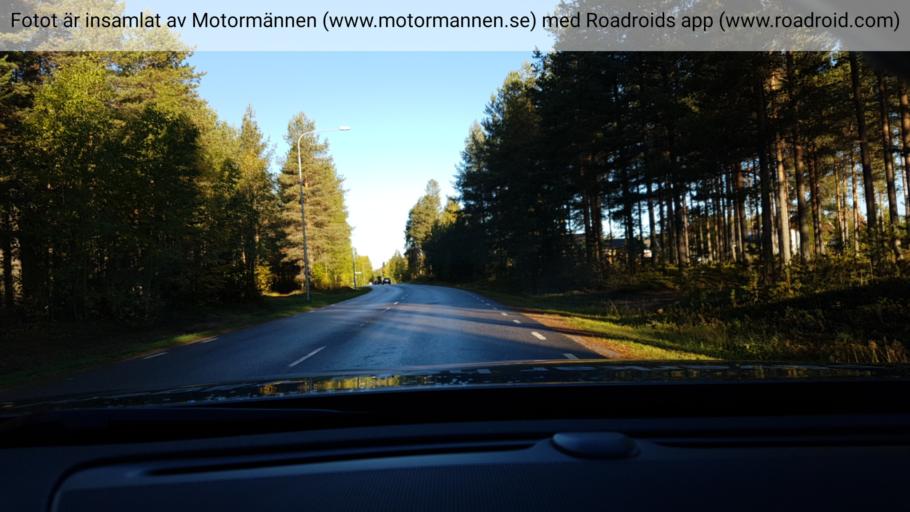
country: SE
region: Norrbotten
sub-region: Lulea Kommun
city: Sodra Sunderbyn
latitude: 65.6514
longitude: 21.9541
